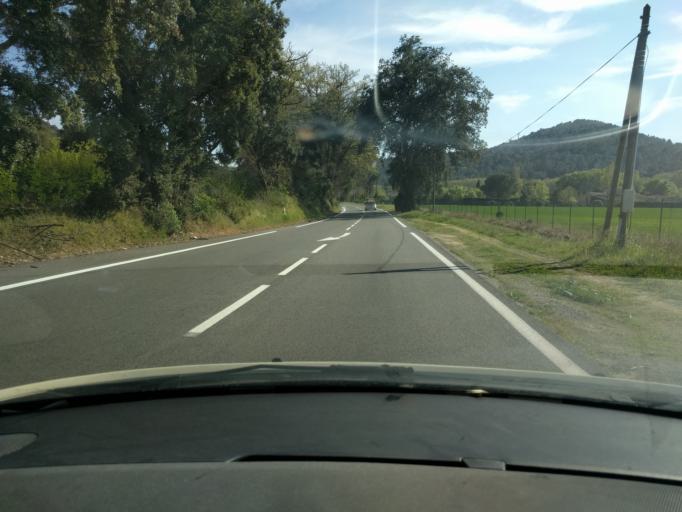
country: FR
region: Provence-Alpes-Cote d'Azur
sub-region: Departement du Var
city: La Crau
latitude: 43.1704
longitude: 6.1184
